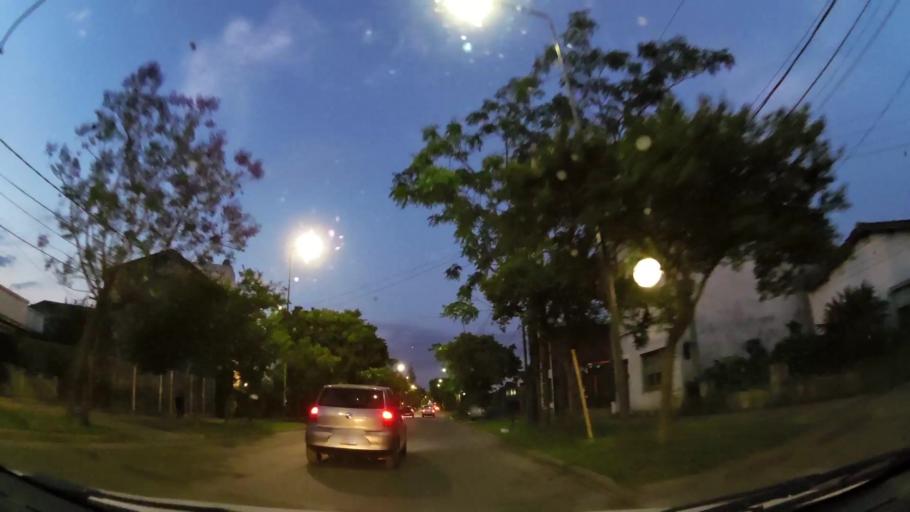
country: AR
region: Buenos Aires
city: Ituzaingo
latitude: -34.6542
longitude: -58.6595
